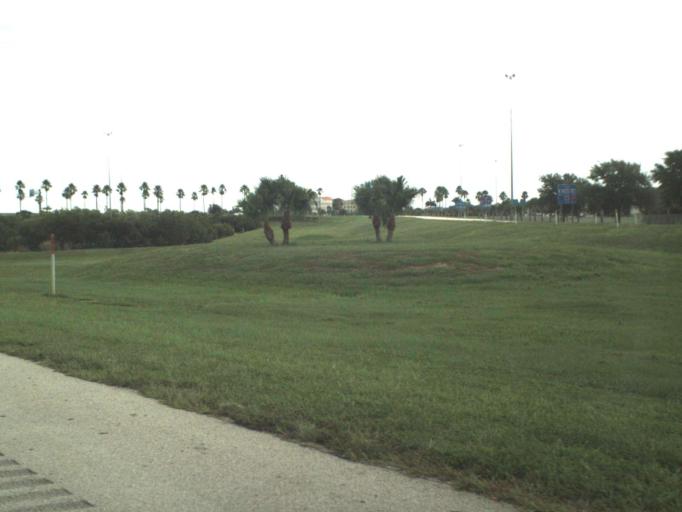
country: US
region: Florida
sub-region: Saint Lucie County
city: Port Saint Lucie
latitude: 27.3084
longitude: -80.4138
